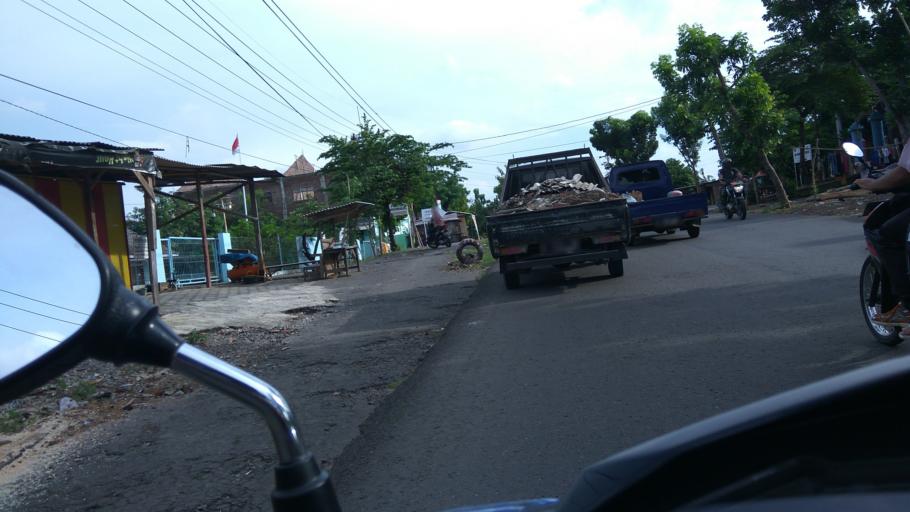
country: ID
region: Central Java
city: Mranggen
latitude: -7.0444
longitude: 110.4609
